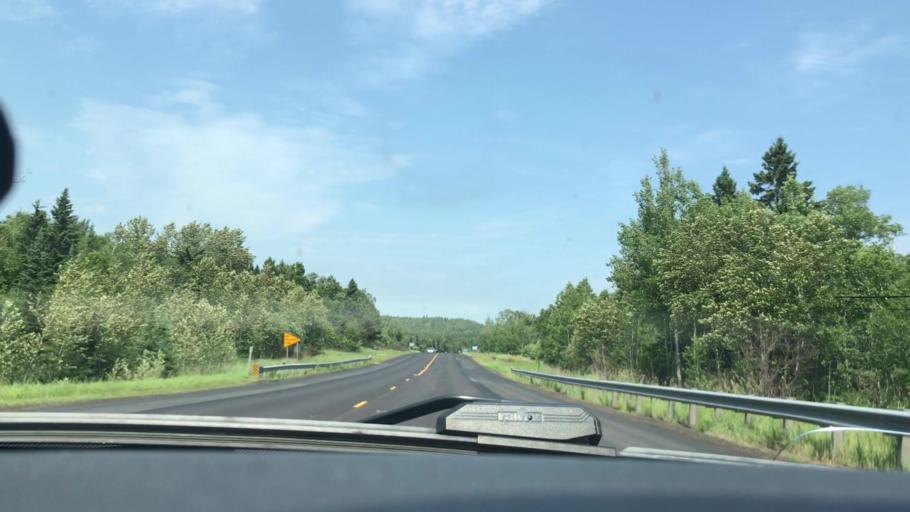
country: US
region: Minnesota
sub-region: Lake County
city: Silver Bay
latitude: 47.3307
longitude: -91.2077
